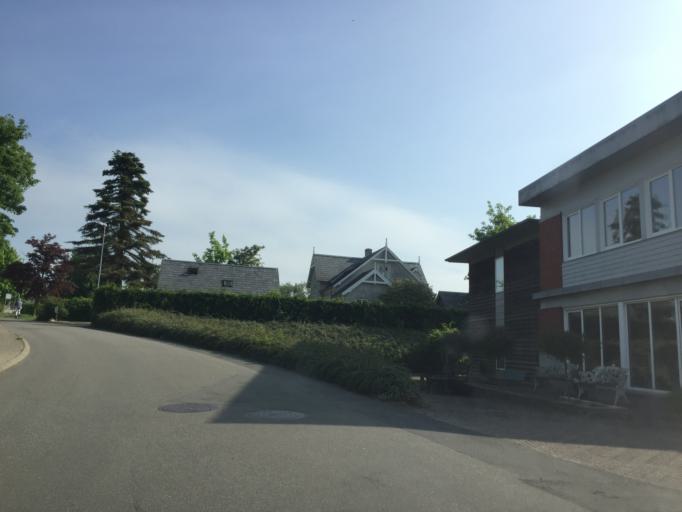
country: DK
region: South Denmark
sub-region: Svendborg Kommune
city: Thuro By
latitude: 55.1371
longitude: 10.7824
